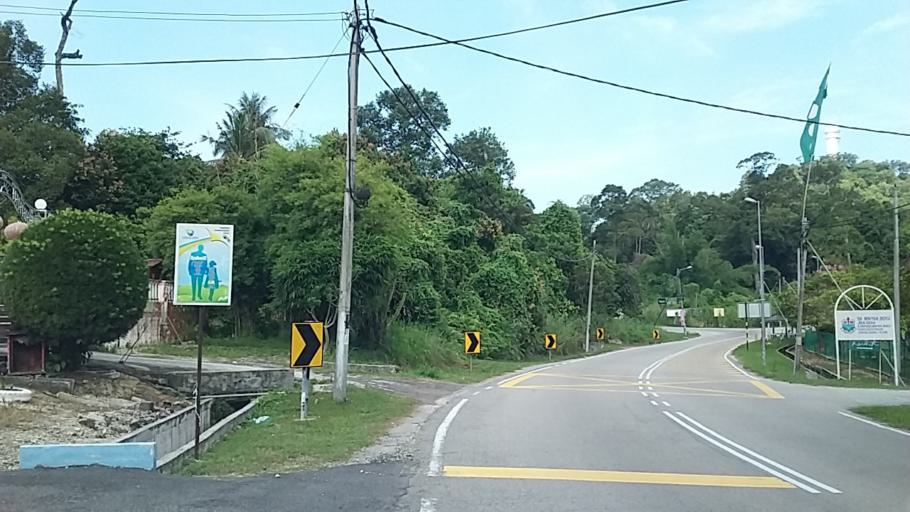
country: MY
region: Johor
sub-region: Daerah Batu Pahat
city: Batu Pahat
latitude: 1.7914
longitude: 102.8940
